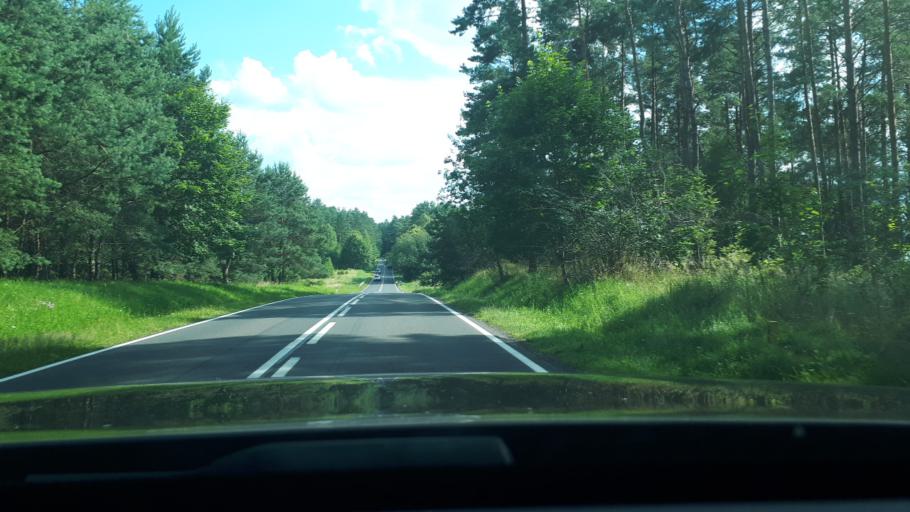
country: PL
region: Warmian-Masurian Voivodeship
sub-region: Powiat olsztynski
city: Stawiguda
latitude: 53.5459
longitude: 20.4193
